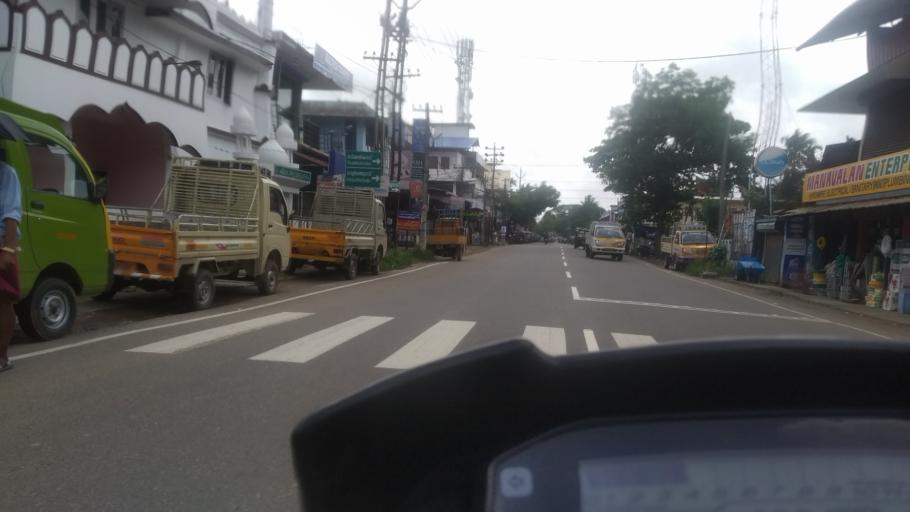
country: IN
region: Kerala
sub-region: Ernakulam
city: Aluva
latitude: 10.1274
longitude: 76.3094
